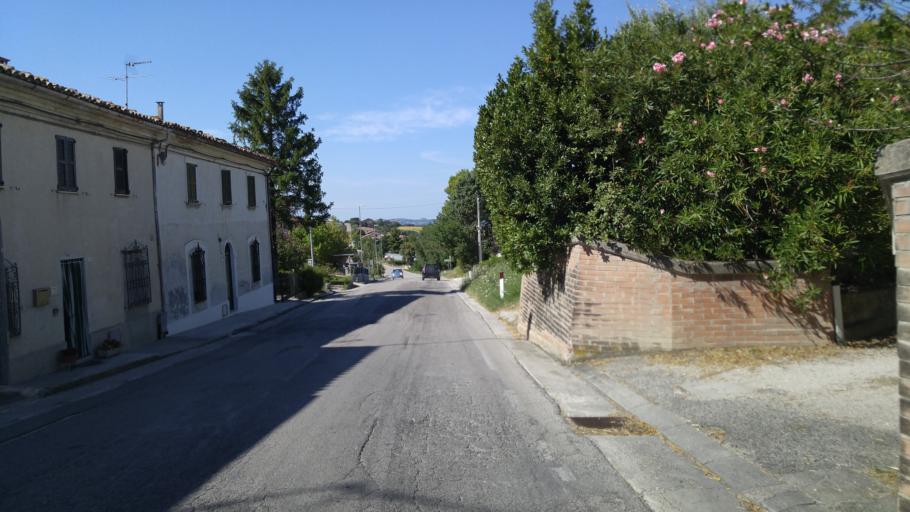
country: IT
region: The Marches
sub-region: Provincia di Pesaro e Urbino
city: San Giorgio di Pesaro
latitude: 43.7191
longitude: 12.9809
